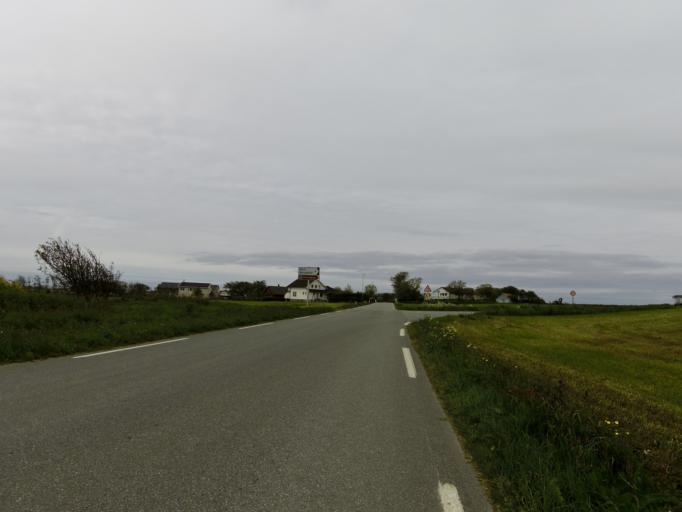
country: NO
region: Rogaland
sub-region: Klepp
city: Kleppe
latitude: 58.8173
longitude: 5.5703
